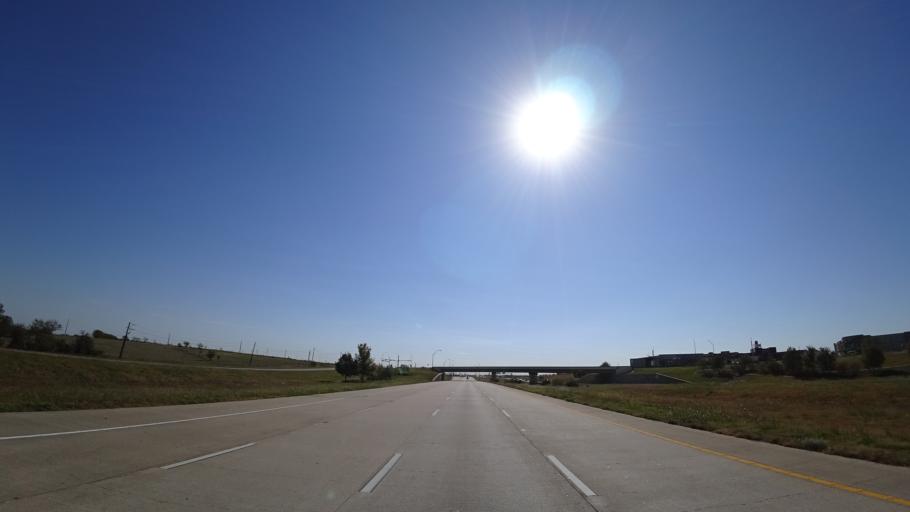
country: US
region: Texas
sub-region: Travis County
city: Pflugerville
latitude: 30.4254
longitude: -97.5882
